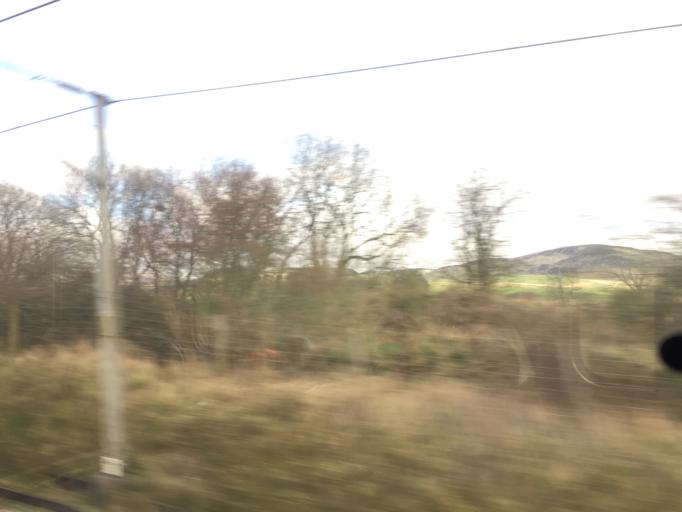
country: GB
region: Scotland
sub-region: Dumfries and Galloway
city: Moffat
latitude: 55.2749
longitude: -3.4179
